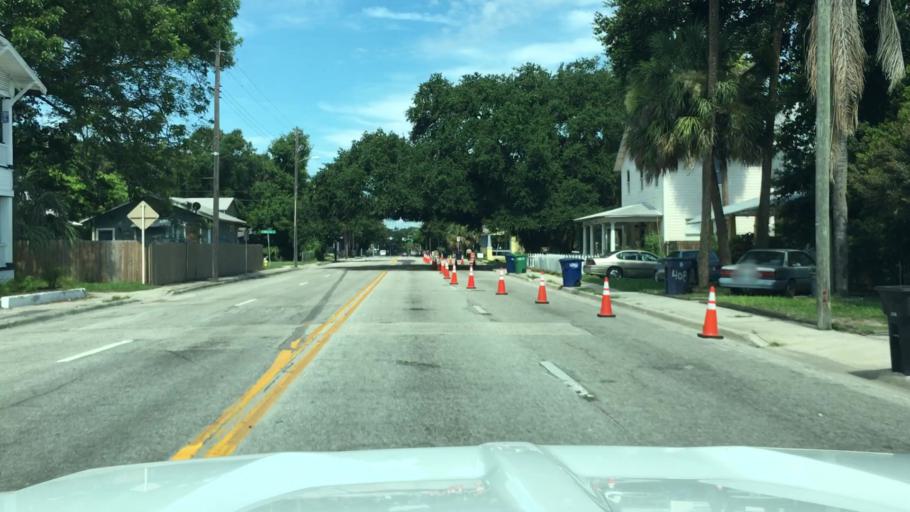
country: US
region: Florida
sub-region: Hillsborough County
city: Tampa
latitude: 27.9709
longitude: -82.4562
